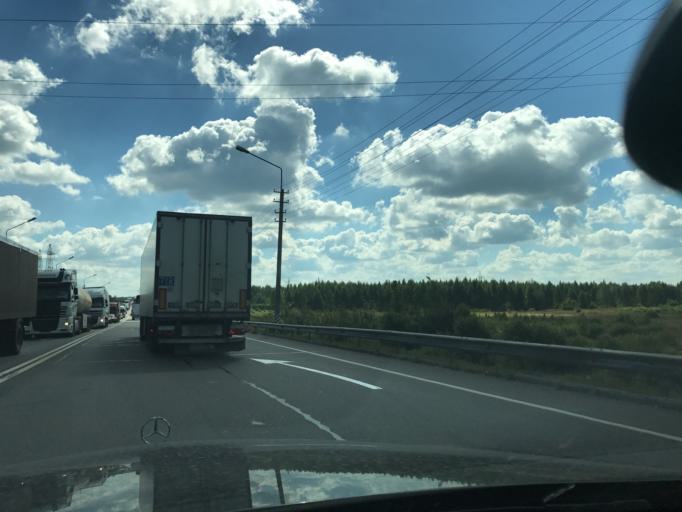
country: RU
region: Vladimir
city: Vorsha
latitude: 56.0793
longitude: 40.2025
